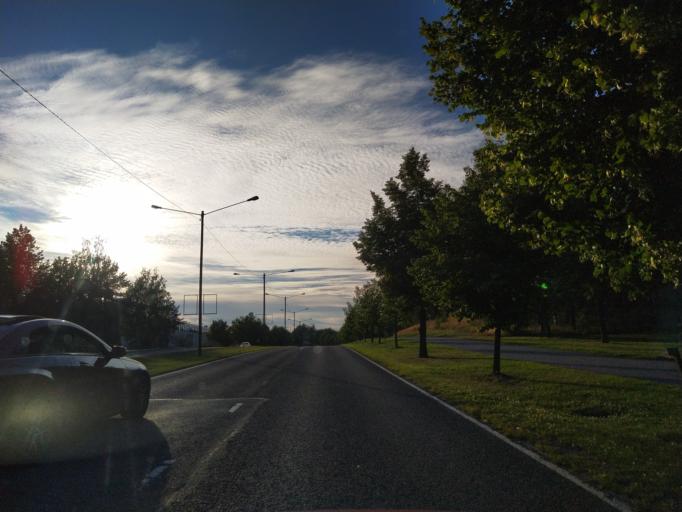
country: FI
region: Varsinais-Suomi
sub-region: Turku
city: Turku
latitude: 60.4468
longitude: 22.3245
